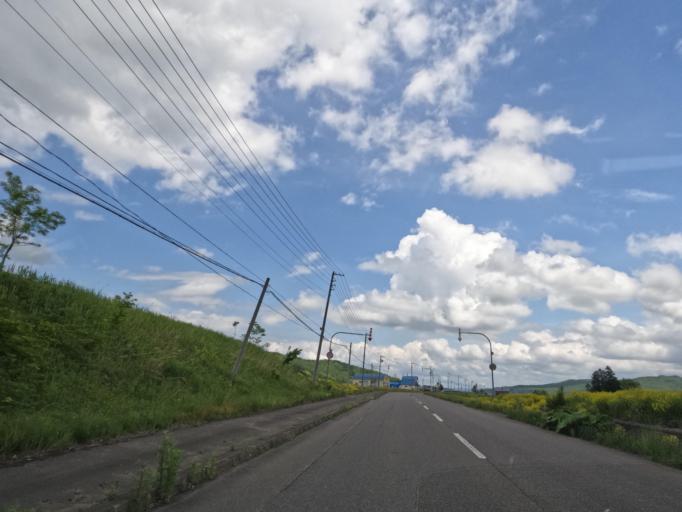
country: JP
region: Hokkaido
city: Takikawa
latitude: 43.5914
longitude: 141.7518
